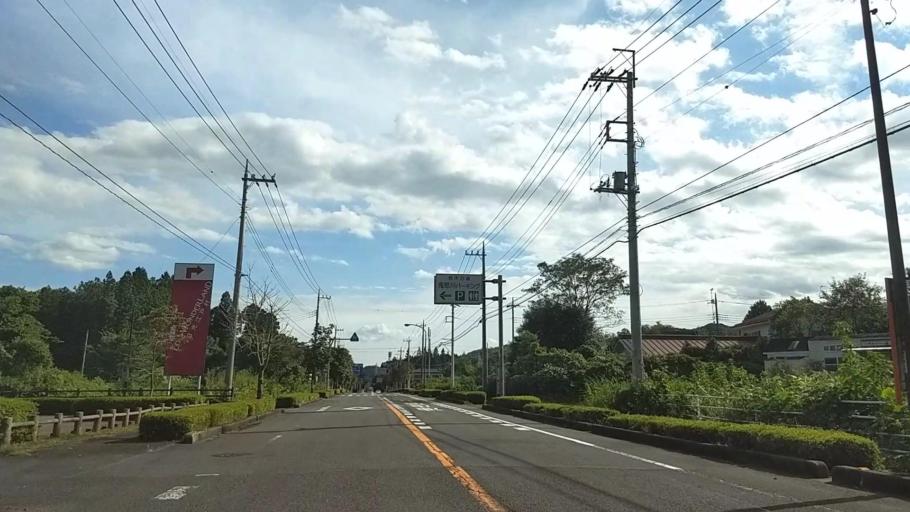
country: JP
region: Tochigi
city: Imaichi
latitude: 36.7969
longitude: 139.7009
